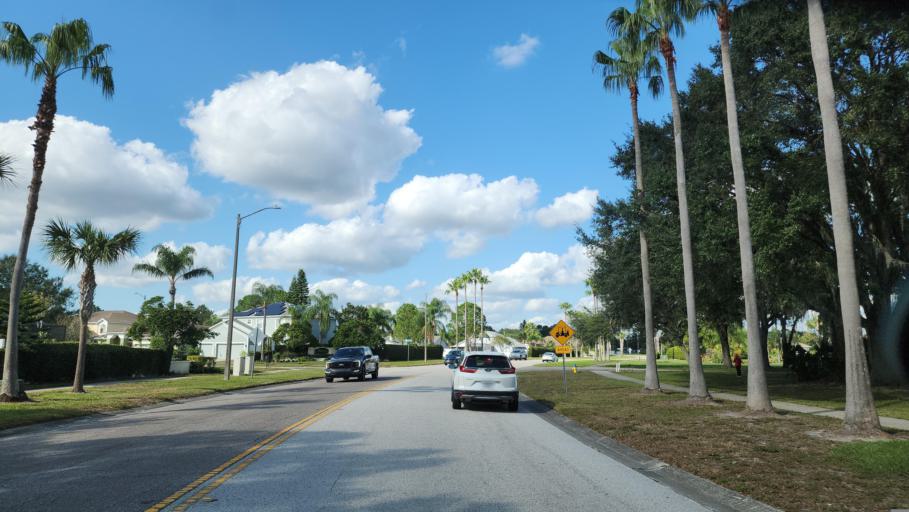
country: US
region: Florida
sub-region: Hillsborough County
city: Balm
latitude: 27.7952
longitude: -82.3183
